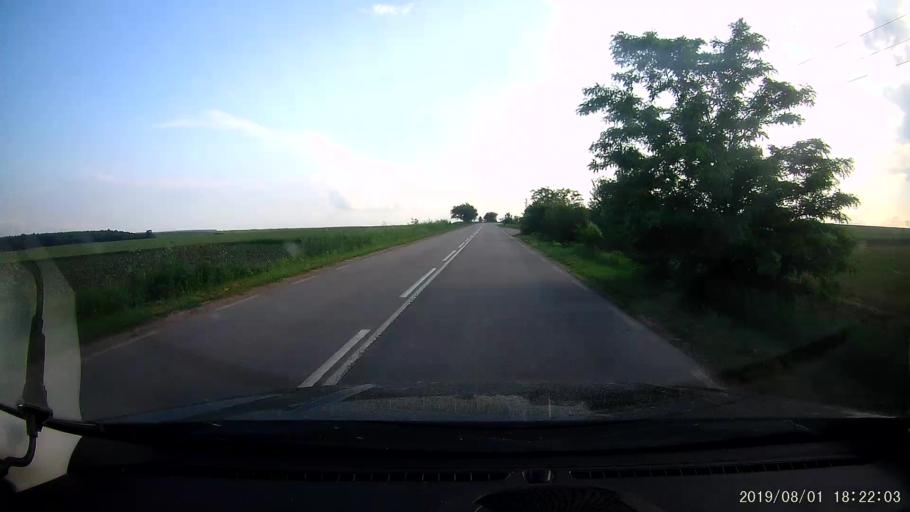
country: BG
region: Shumen
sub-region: Obshtina Kaolinovo
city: Kaolinovo
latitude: 43.6427
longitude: 27.0597
